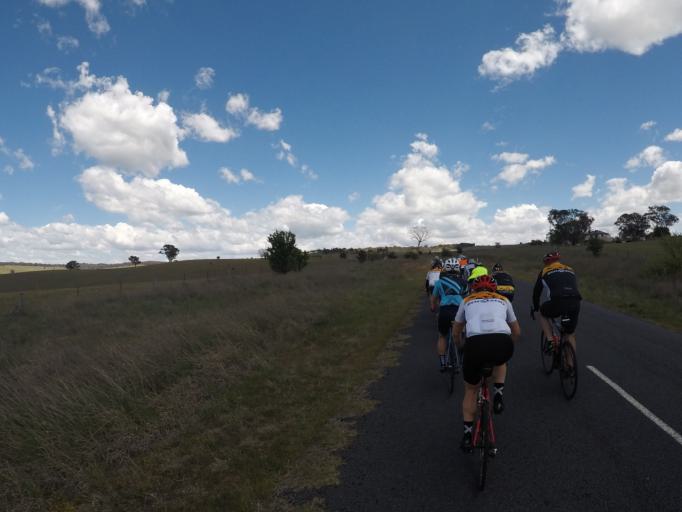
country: AU
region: New South Wales
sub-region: Blayney
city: Blayney
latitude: -33.5704
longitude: 149.4089
